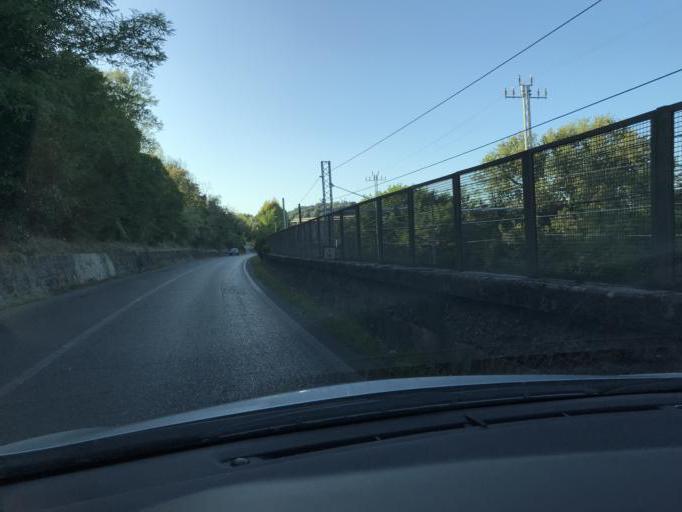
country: IT
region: Latium
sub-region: Provincia di Viterbo
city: Orte
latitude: 42.4470
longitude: 12.3935
